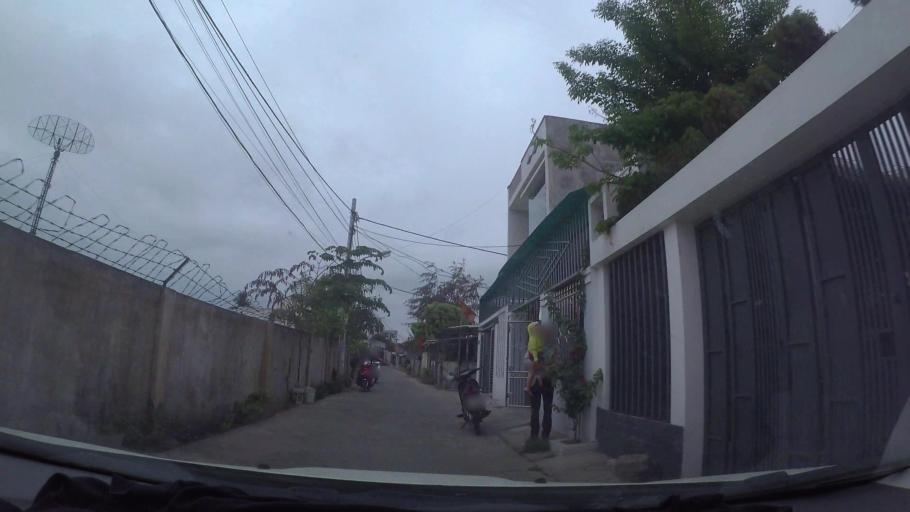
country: VN
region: Da Nang
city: Lien Chieu
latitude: 16.0845
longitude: 108.1540
